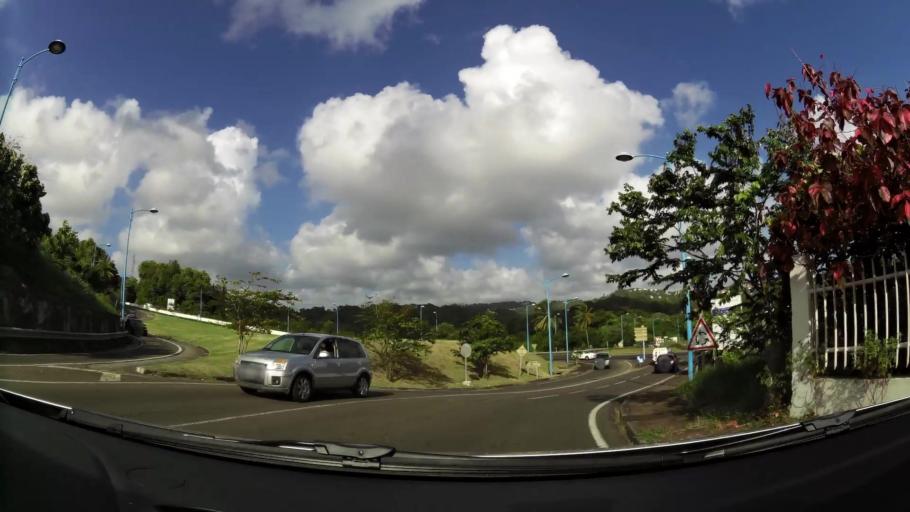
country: MQ
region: Martinique
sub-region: Martinique
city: Le Robert
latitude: 14.6739
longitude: -60.9468
